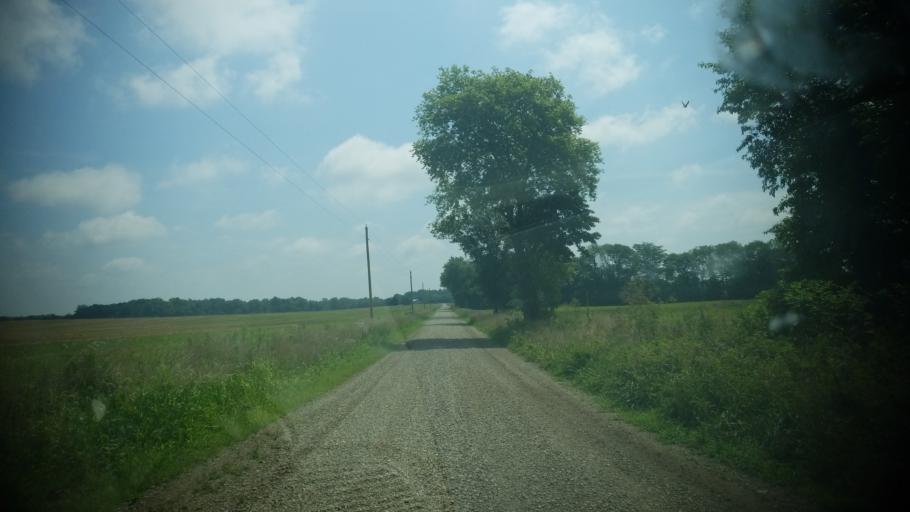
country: US
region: Illinois
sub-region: Wayne County
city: Fairfield
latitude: 38.5298
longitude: -88.3749
